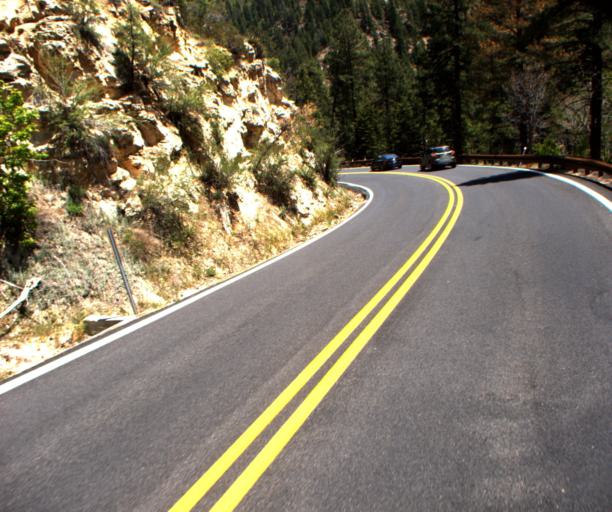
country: US
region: Arizona
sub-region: Coconino County
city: Kachina Village
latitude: 35.0253
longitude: -111.7394
